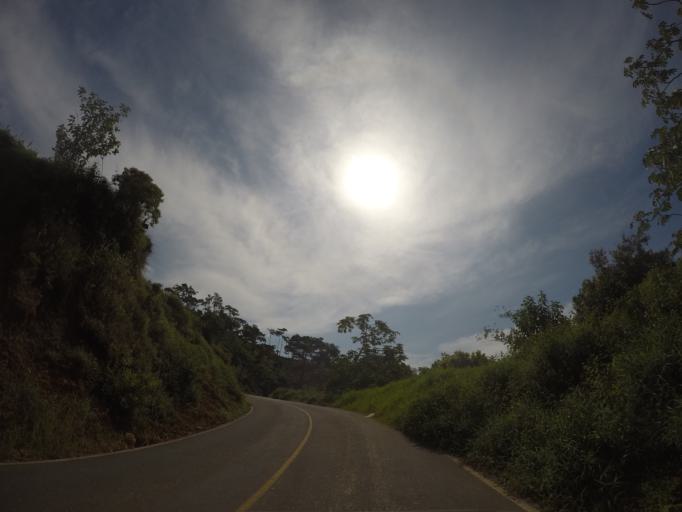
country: MX
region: Oaxaca
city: Pluma Hidalgo
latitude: 15.9310
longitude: -96.4230
